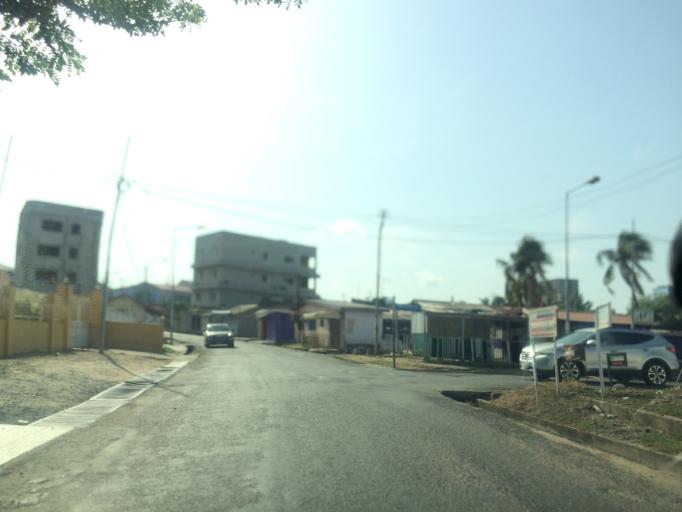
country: GH
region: Greater Accra
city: Accra
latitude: 5.5575
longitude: -0.1790
